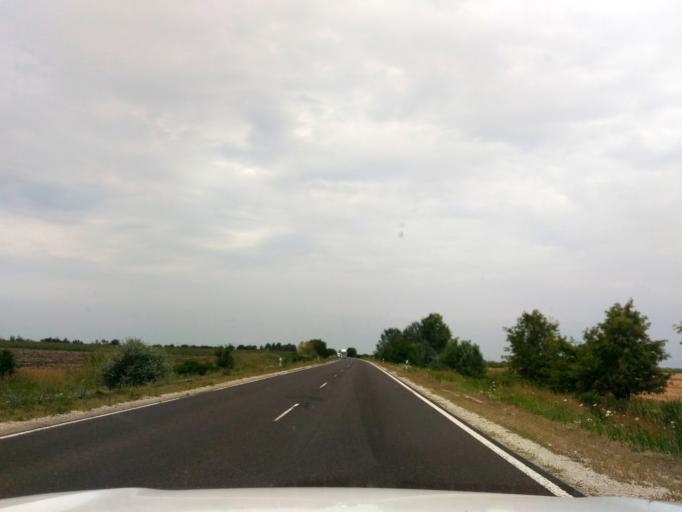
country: HU
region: Pest
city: Abony
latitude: 47.2027
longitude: 20.0754
